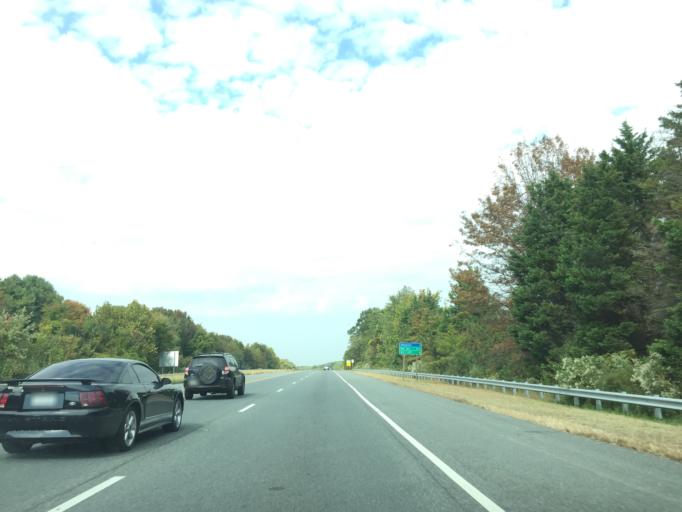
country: US
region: Maryland
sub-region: Harford County
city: Bel Air South
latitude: 39.4713
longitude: -76.3162
